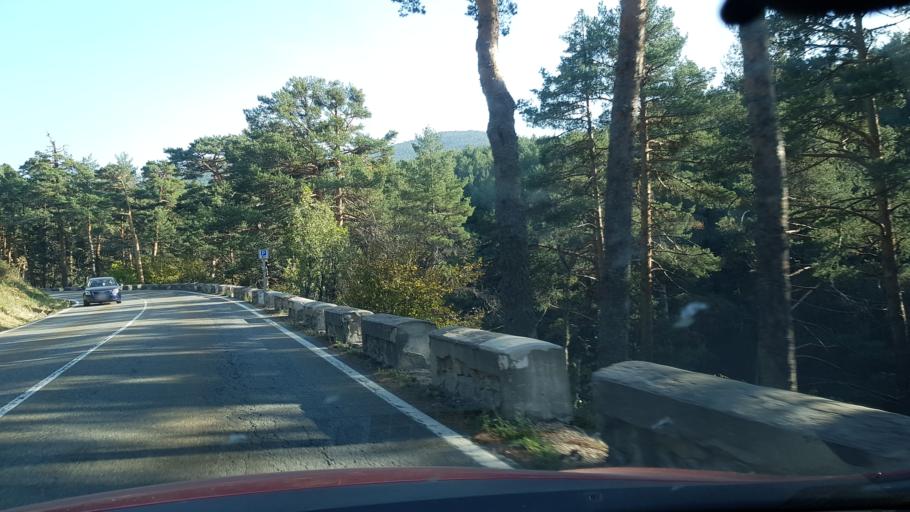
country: ES
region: Castille and Leon
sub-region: Provincia de Segovia
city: San Ildefonso
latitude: 40.8242
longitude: -4.0195
